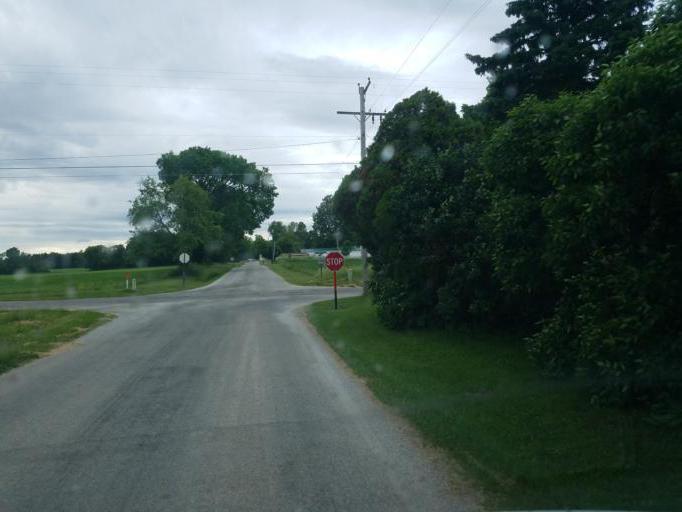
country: US
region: Ohio
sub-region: Morrow County
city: Mount Gilead
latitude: 40.5567
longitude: -82.8718
